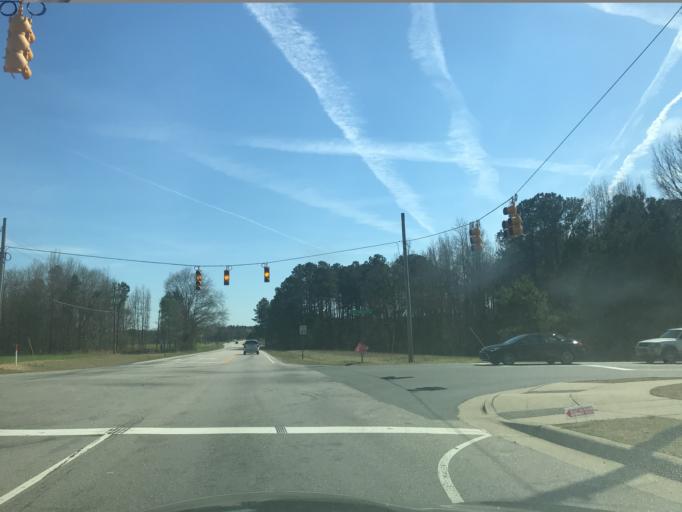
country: US
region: North Carolina
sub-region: Wake County
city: Fuquay-Varina
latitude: 35.5888
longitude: -78.7732
